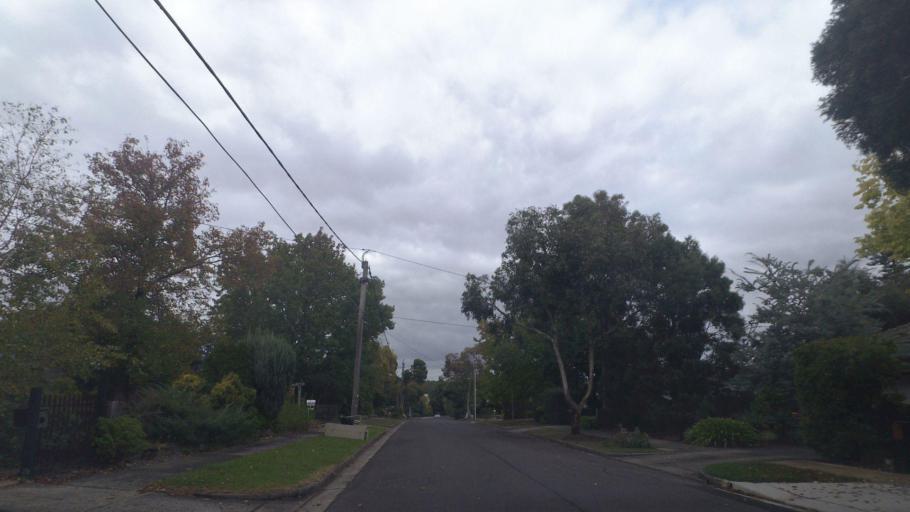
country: AU
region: Victoria
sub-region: Whitehorse
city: Forest Hill
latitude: -37.8312
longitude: 145.1688
